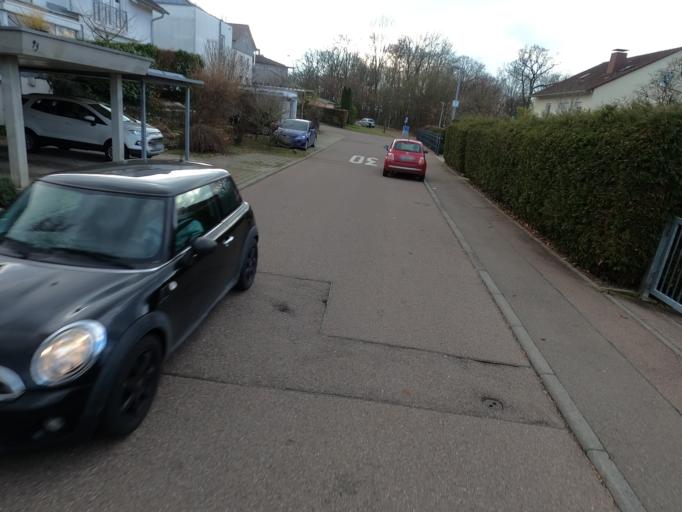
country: DE
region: Baden-Wuerttemberg
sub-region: Regierungsbezirk Stuttgart
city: Goeppingen
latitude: 48.6946
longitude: 9.6373
